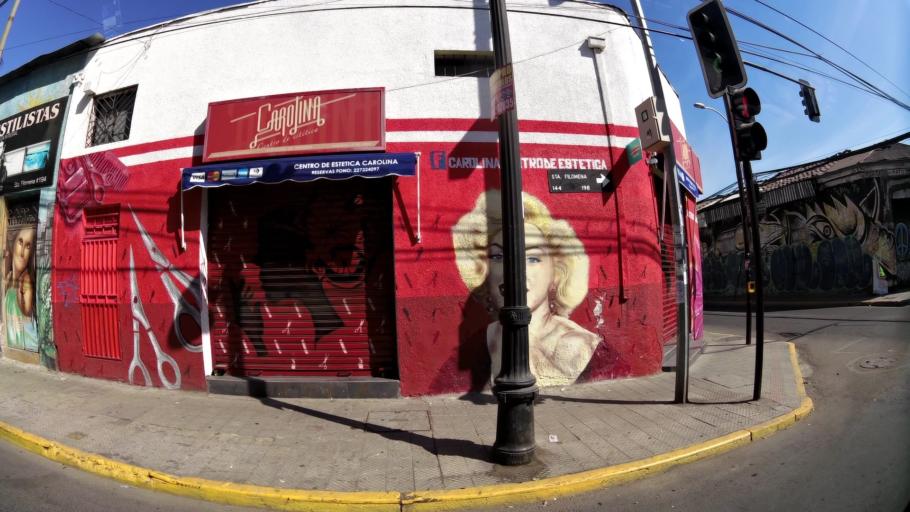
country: CL
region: Santiago Metropolitan
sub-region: Provincia de Santiago
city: Santiago
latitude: -33.4303
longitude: -70.6419
